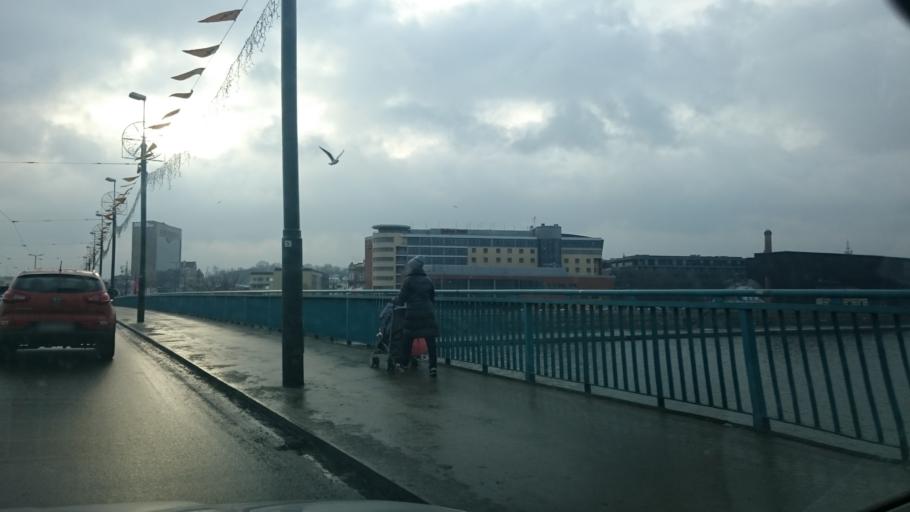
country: PL
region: Lesser Poland Voivodeship
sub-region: Krakow
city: Krakow
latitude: 50.0498
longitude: 19.9525
